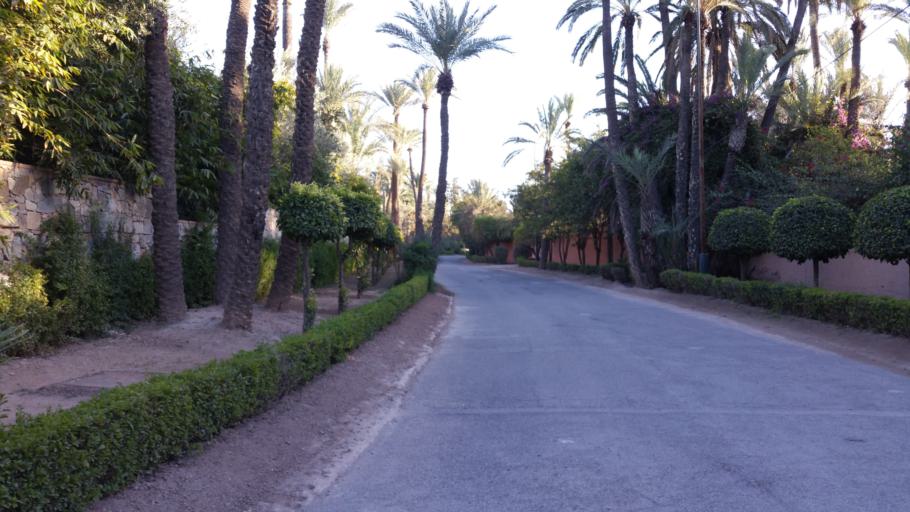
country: MA
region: Marrakech-Tensift-Al Haouz
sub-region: Marrakech
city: Marrakesh
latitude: 31.6535
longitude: -7.9788
